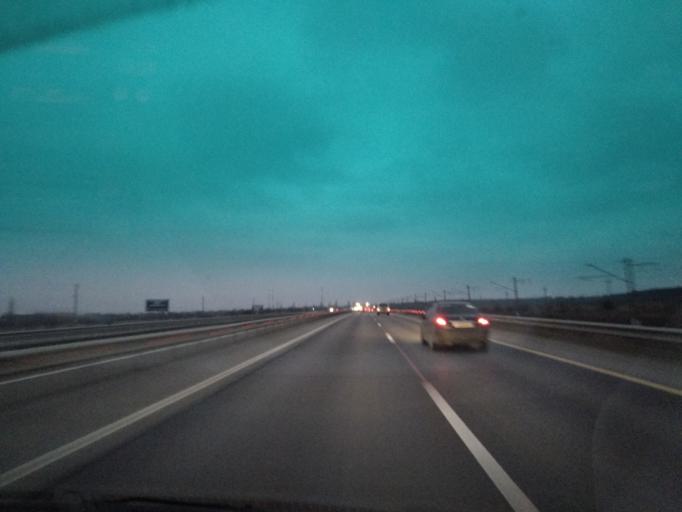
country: RU
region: Adygeya
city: Adygeysk
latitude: 44.8171
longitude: 39.2268
